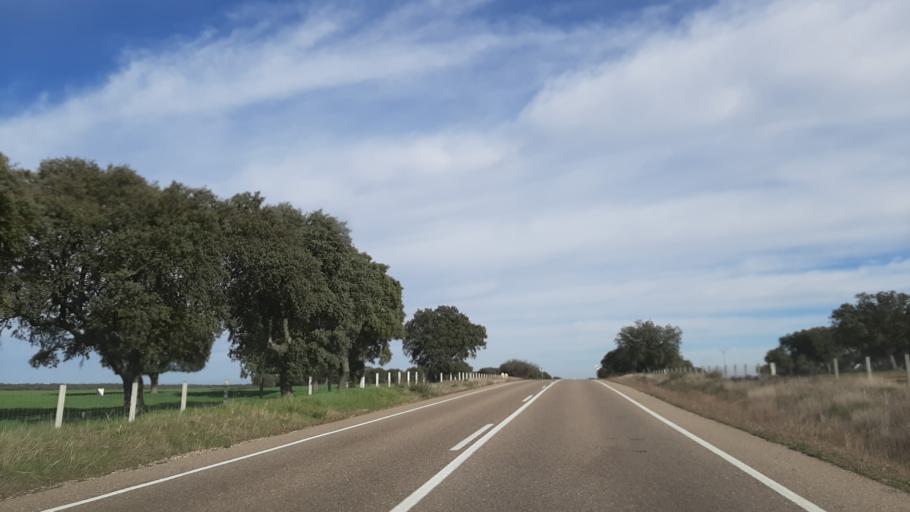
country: ES
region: Castille and Leon
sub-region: Provincia de Salamanca
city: Anover de Tormes
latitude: 41.0895
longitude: -5.9362
